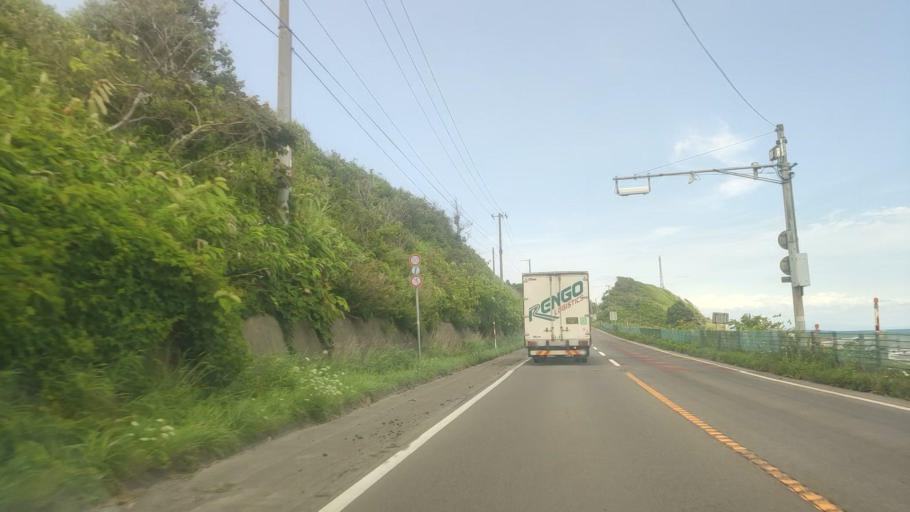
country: JP
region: Hokkaido
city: Nanae
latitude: 42.1660
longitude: 140.4627
